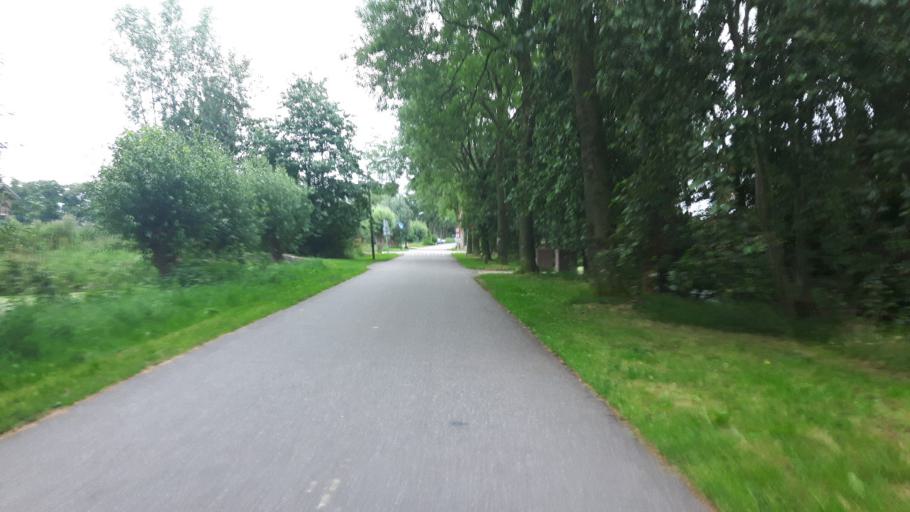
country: NL
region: Utrecht
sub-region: Gemeente Woerden
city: Woerden
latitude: 52.0784
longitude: 4.9147
